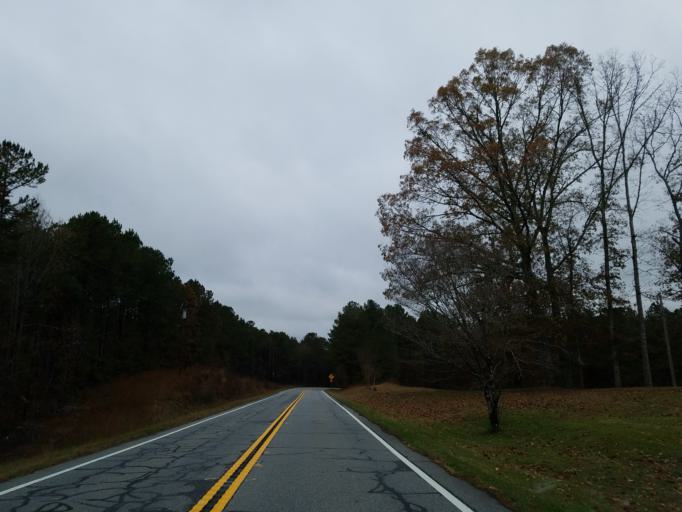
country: US
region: Georgia
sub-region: Cherokee County
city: Canton
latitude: 34.2586
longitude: -84.6000
